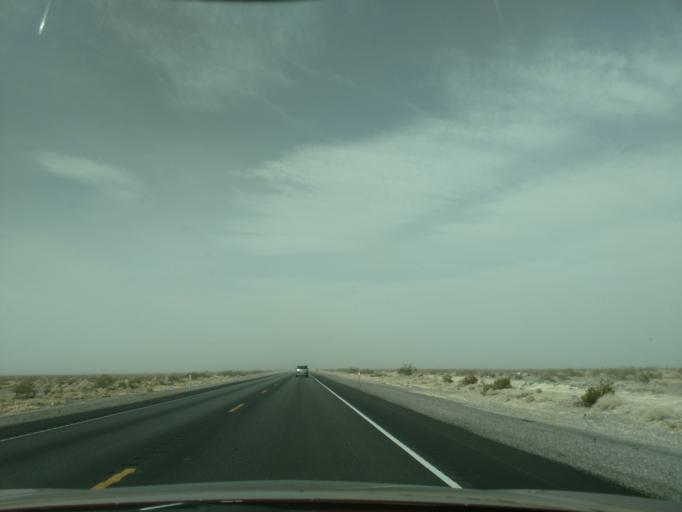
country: US
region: Nevada
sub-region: Nye County
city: Beatty
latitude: 36.6352
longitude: -116.3652
